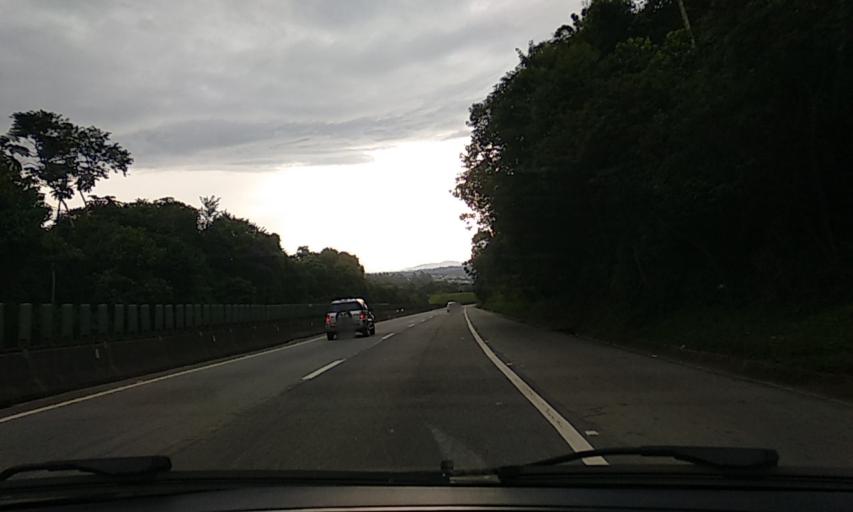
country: BR
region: Sao Paulo
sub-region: Mogi das Cruzes
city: Mogi das Cruzes
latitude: -23.4774
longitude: -46.2379
